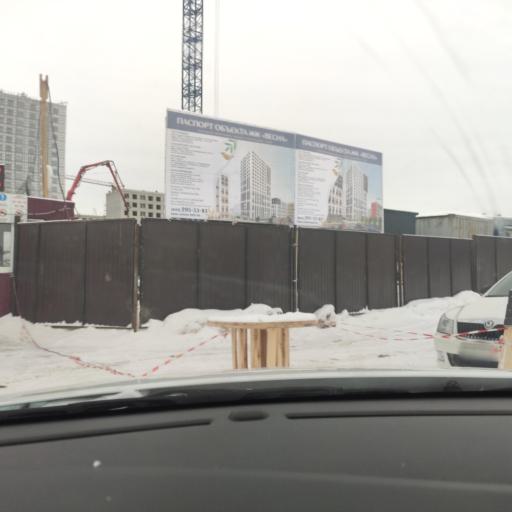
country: RU
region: Tatarstan
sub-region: Gorod Kazan'
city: Kazan
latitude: 55.7877
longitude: 49.2517
